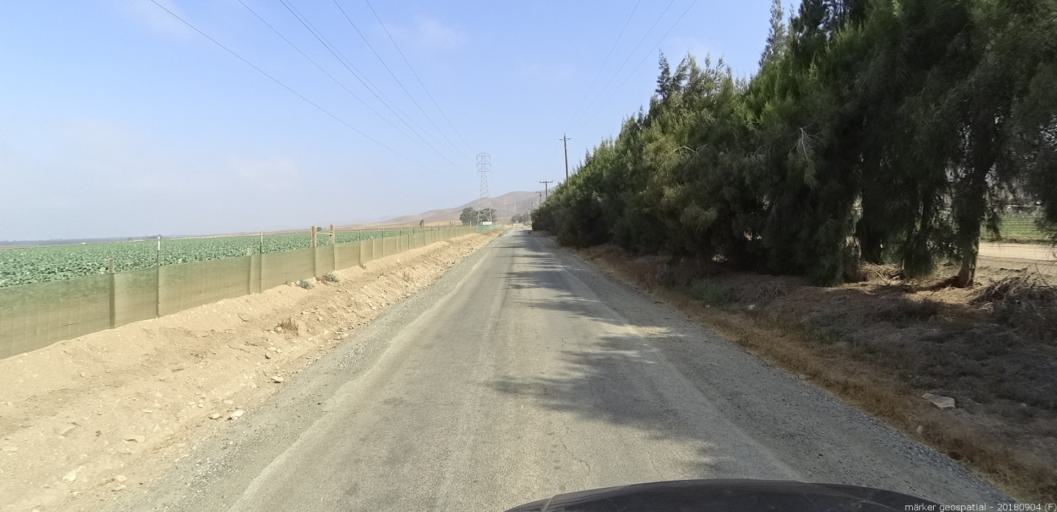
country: US
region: California
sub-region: Monterey County
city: Soledad
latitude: 36.4585
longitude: -121.3317
